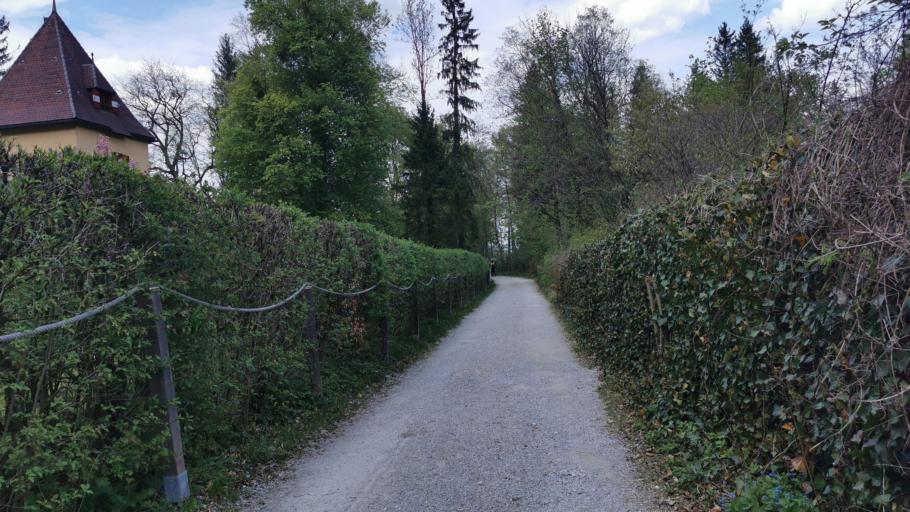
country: AT
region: Salzburg
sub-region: Politischer Bezirk Salzburg-Umgebung
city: Grodig
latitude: 47.7449
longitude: 13.0121
